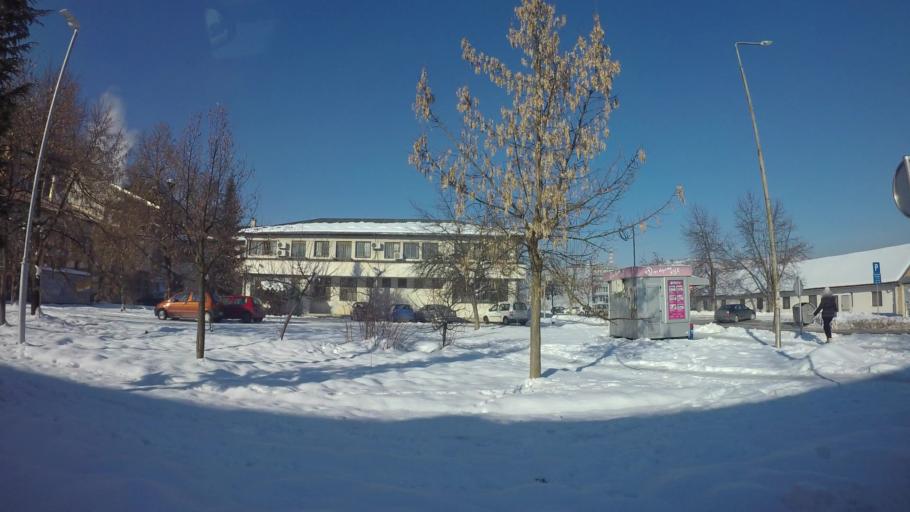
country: BA
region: Federation of Bosnia and Herzegovina
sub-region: Kanton Sarajevo
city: Sarajevo
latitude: 43.8244
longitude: 18.3687
